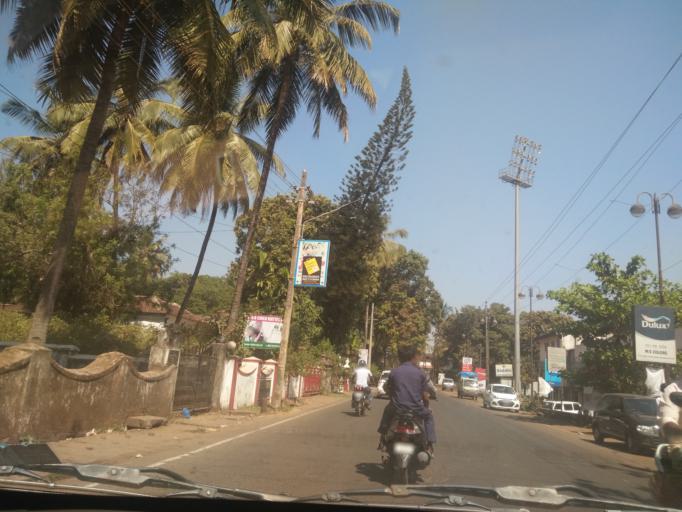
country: IN
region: Goa
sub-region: North Goa
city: Mapuca
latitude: 15.5985
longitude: 73.8155
